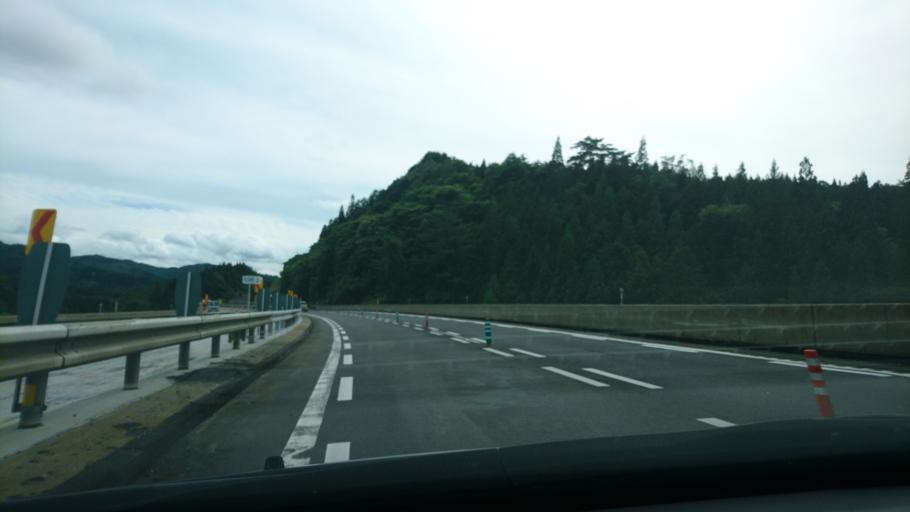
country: JP
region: Iwate
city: Ichinohe
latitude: 40.2245
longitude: 141.3621
